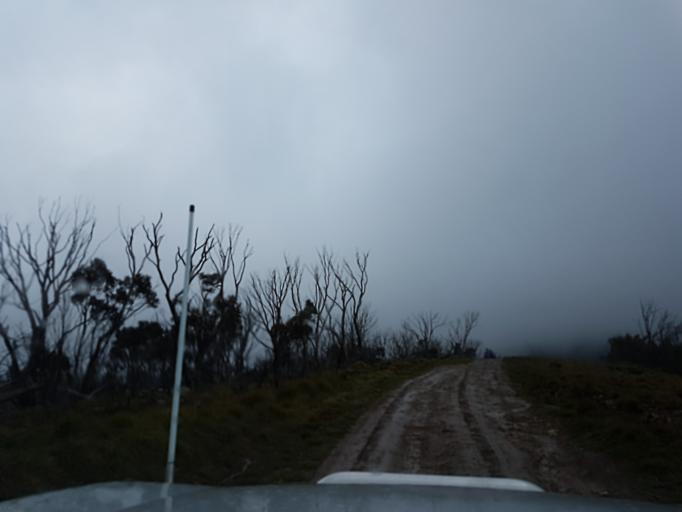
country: AU
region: Victoria
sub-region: Alpine
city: Mount Beauty
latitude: -37.0872
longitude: 147.1050
